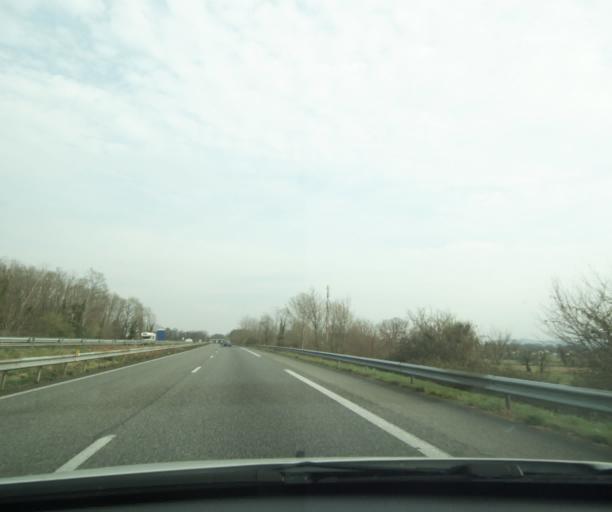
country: FR
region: Aquitaine
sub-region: Departement des Pyrenees-Atlantiques
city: Poey-de-Lescar
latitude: 43.3611
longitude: -0.4698
